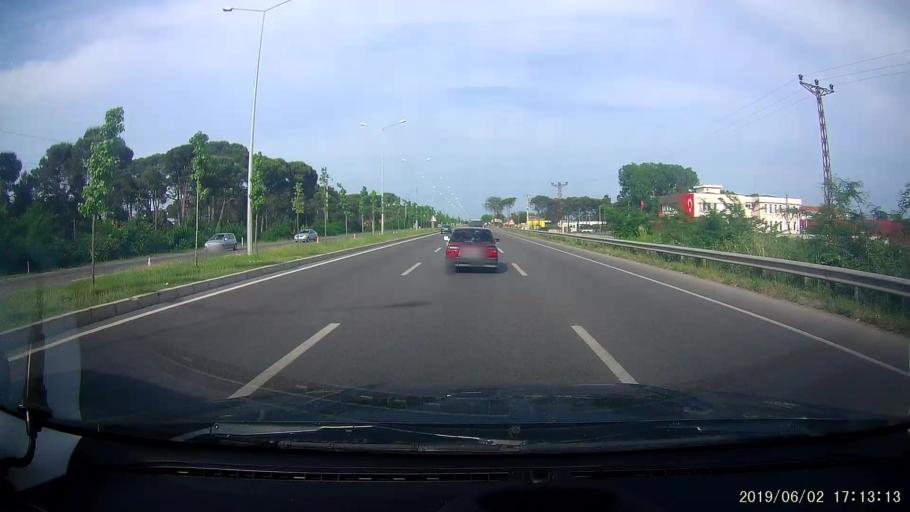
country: TR
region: Samsun
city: Tekkekoy
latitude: 41.2305
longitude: 36.5032
